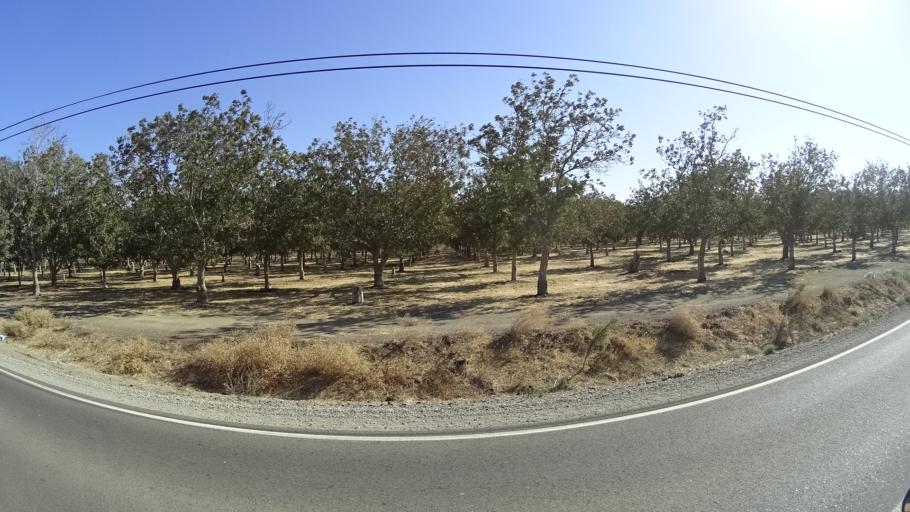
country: US
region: California
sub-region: Yolo County
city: Cottonwood
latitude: 38.6300
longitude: -121.9714
